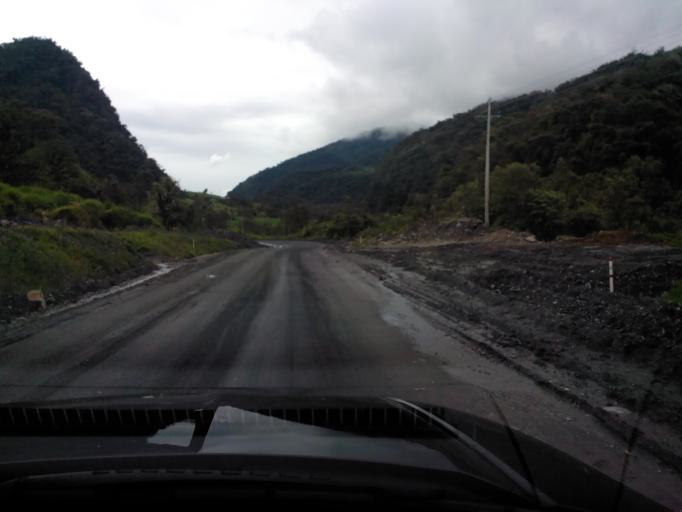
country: EC
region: Napo
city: Archidona
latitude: -0.5076
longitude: -77.8790
